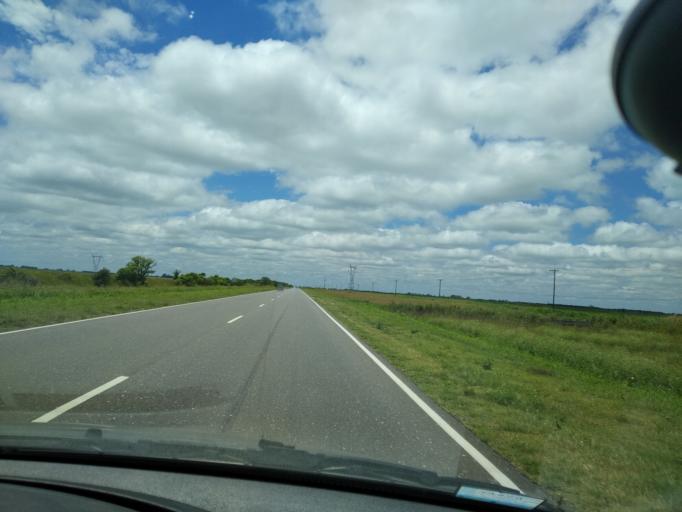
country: AR
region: Cordoba
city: Toledo
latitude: -31.6463
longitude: -64.0449
